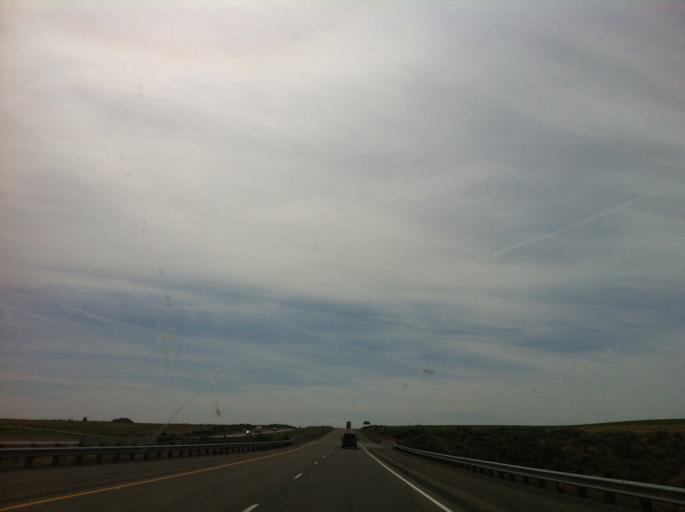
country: US
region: Oregon
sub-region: Malheur County
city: Ontario
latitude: 44.0982
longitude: -117.0376
